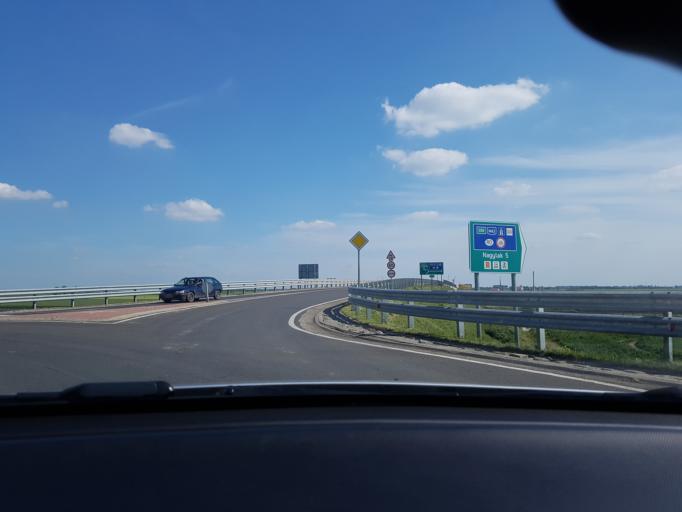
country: HU
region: Csongrad
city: Csanadpalota
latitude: 46.2170
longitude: 20.7144
